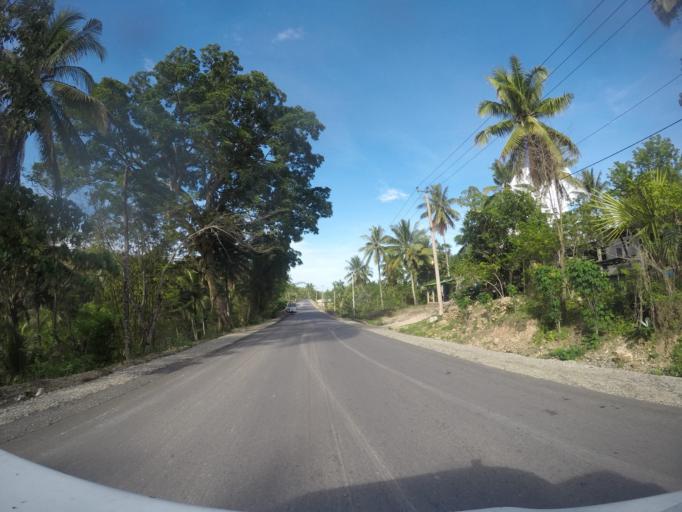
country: TL
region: Baucau
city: Baucau
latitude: -8.5007
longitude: 126.4496
